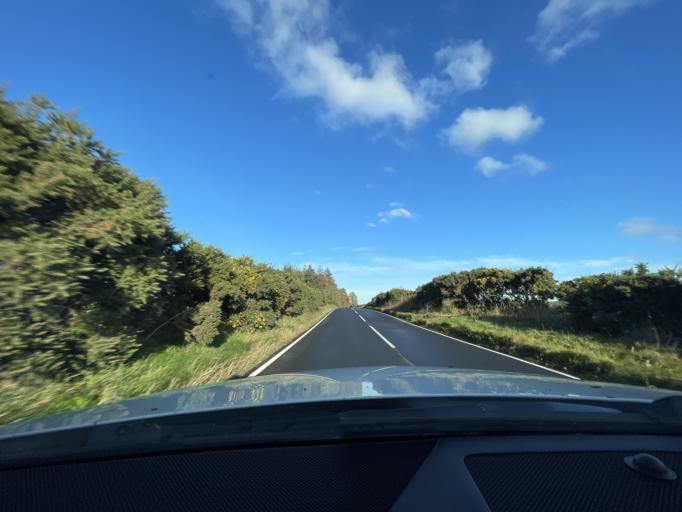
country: GB
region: Scotland
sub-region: Highland
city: Inverness
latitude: 57.4060
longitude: -4.3140
